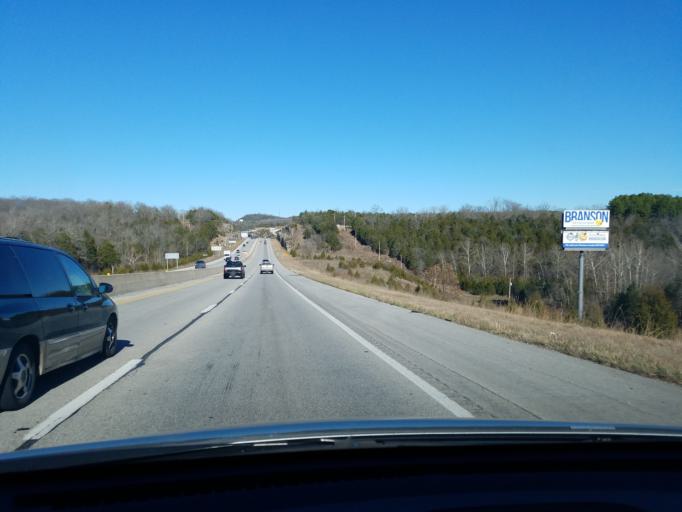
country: US
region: Missouri
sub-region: Taney County
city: Merriam Woods
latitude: 36.7248
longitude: -93.2206
